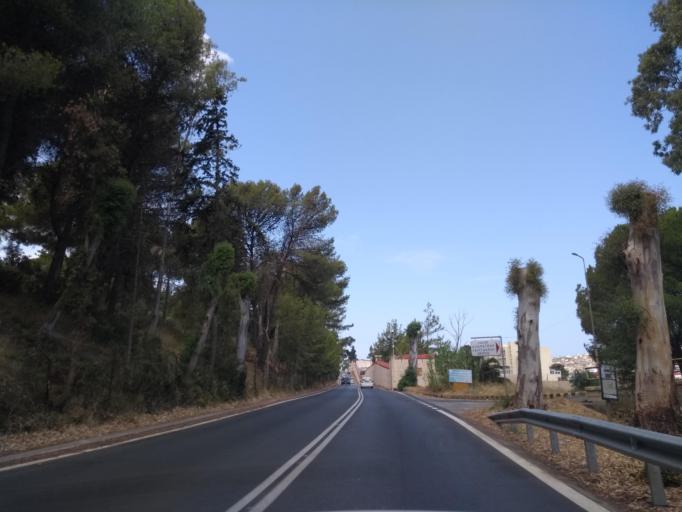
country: GR
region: Crete
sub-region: Nomos Chanias
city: Souda
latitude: 35.4854
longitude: 24.0855
